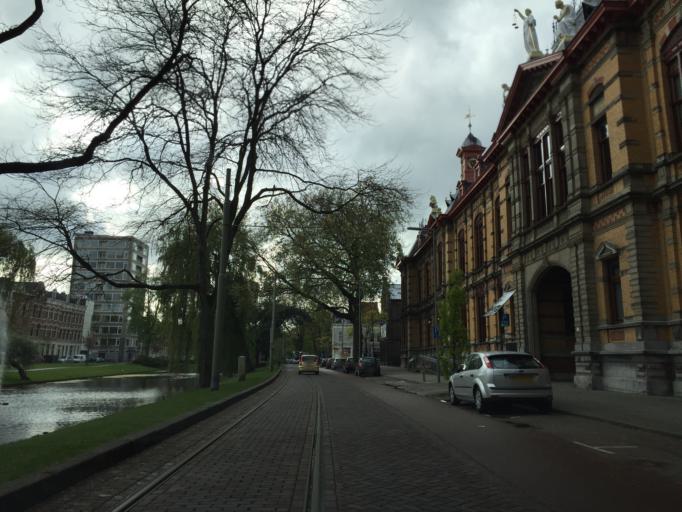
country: NL
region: South Holland
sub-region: Gemeente Rotterdam
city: Rotterdam
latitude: 51.9314
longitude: 4.4771
